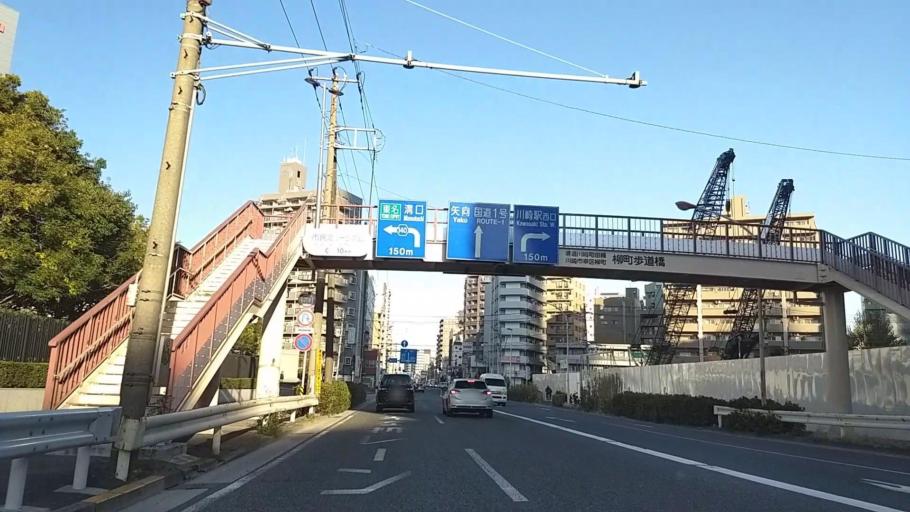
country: JP
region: Kanagawa
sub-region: Kawasaki-shi
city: Kawasaki
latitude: 35.5297
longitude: 139.6917
